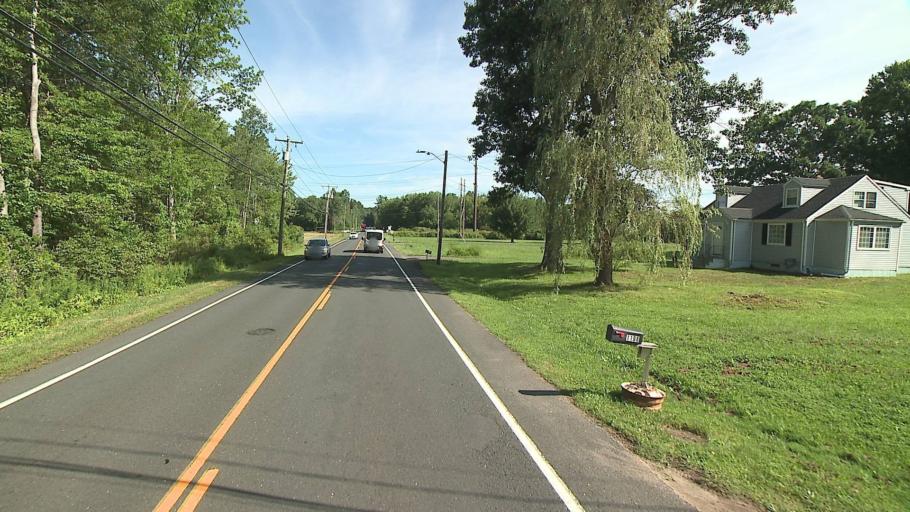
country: US
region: Connecticut
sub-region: Hartford County
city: Blue Hills
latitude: 41.8416
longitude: -72.7000
